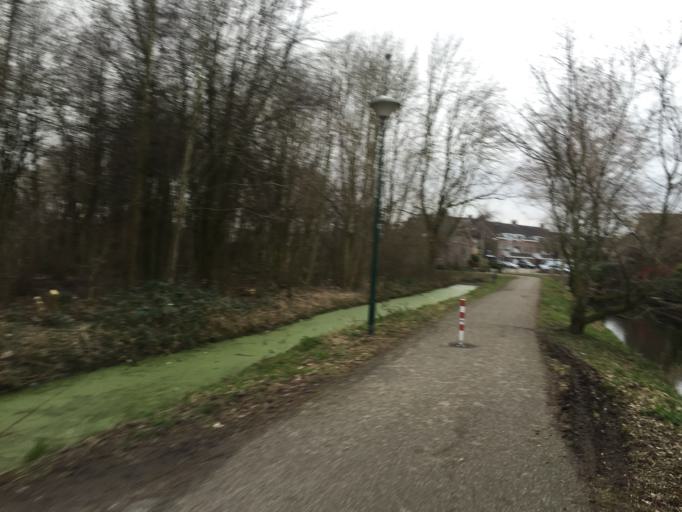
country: NL
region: Utrecht
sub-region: Gemeente Oudewater
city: Oudewater
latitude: 52.0191
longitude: 4.8756
